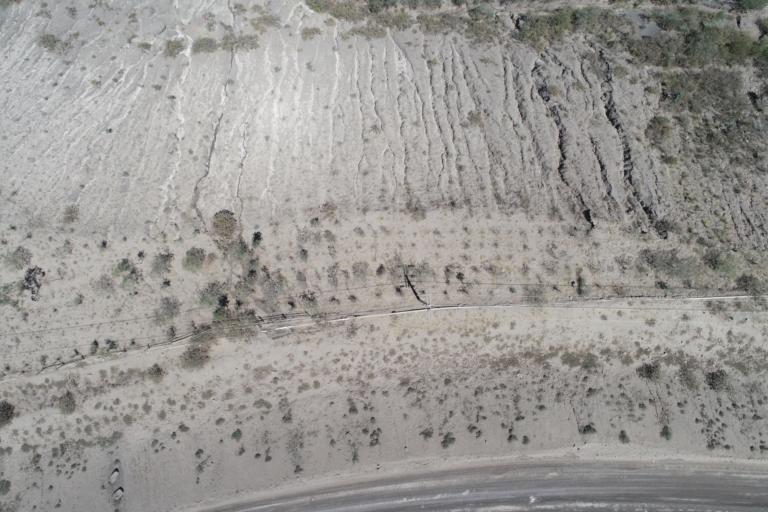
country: BO
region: La Paz
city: La Paz
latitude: -16.6133
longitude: -68.0608
